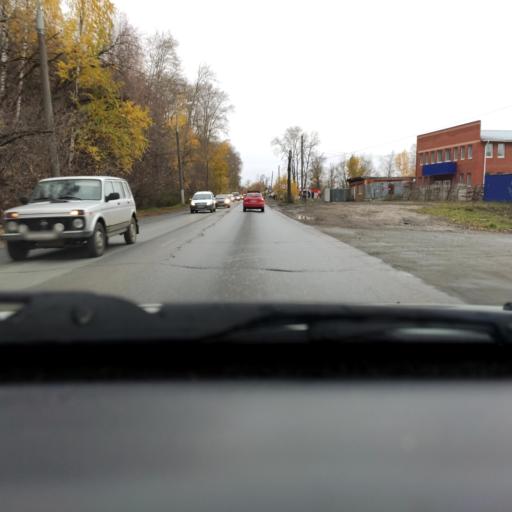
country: RU
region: Perm
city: Perm
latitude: 58.0679
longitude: 56.3453
